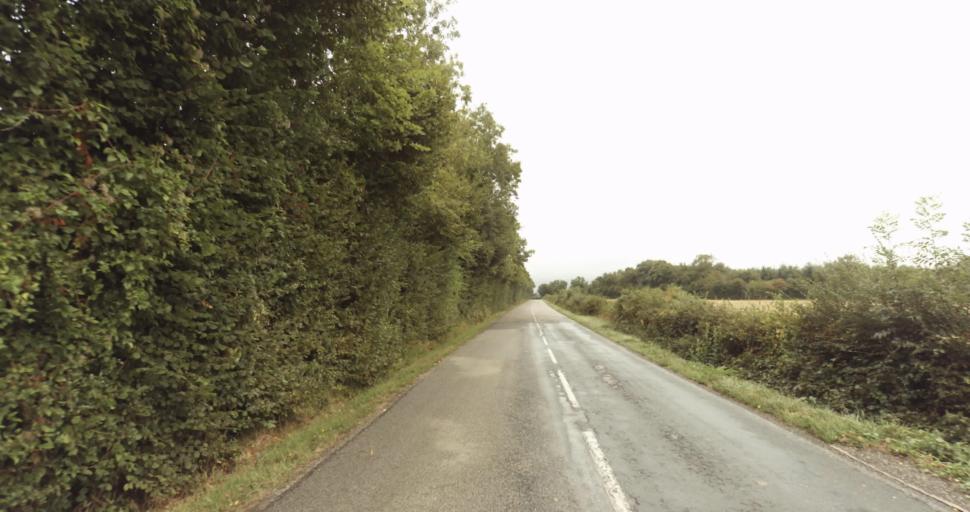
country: FR
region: Lower Normandy
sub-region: Departement de l'Orne
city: Vimoutiers
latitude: 48.8718
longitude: 0.1874
